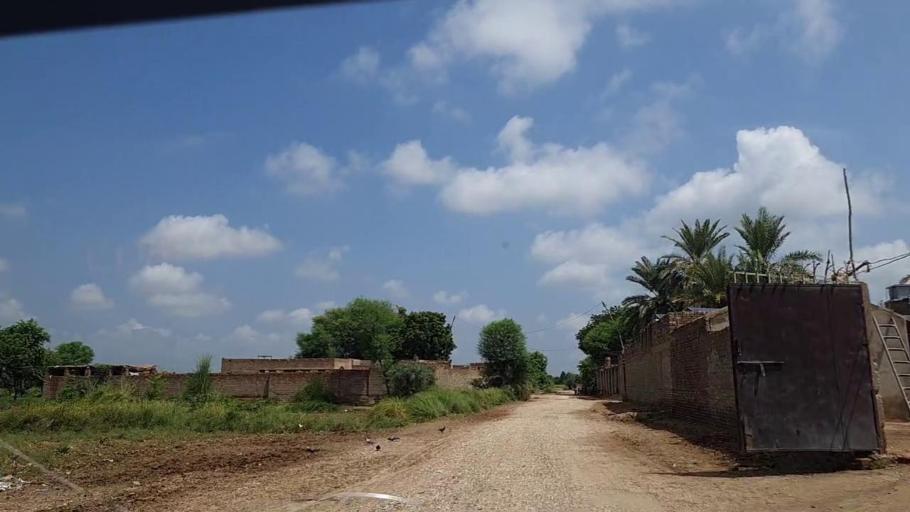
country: PK
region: Sindh
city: Tharu Shah
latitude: 26.8982
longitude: 68.0397
